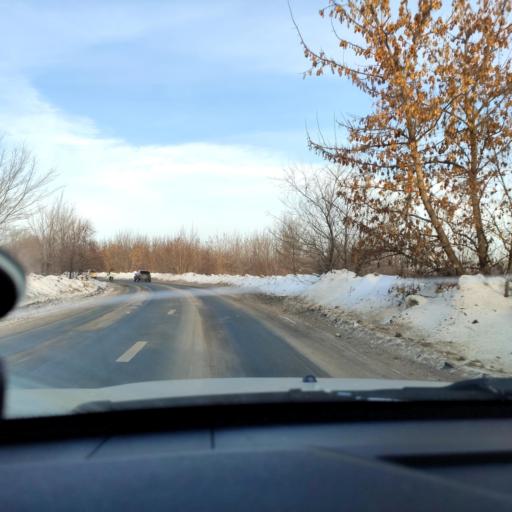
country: RU
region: Samara
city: Smyshlyayevka
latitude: 53.2459
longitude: 50.3643
